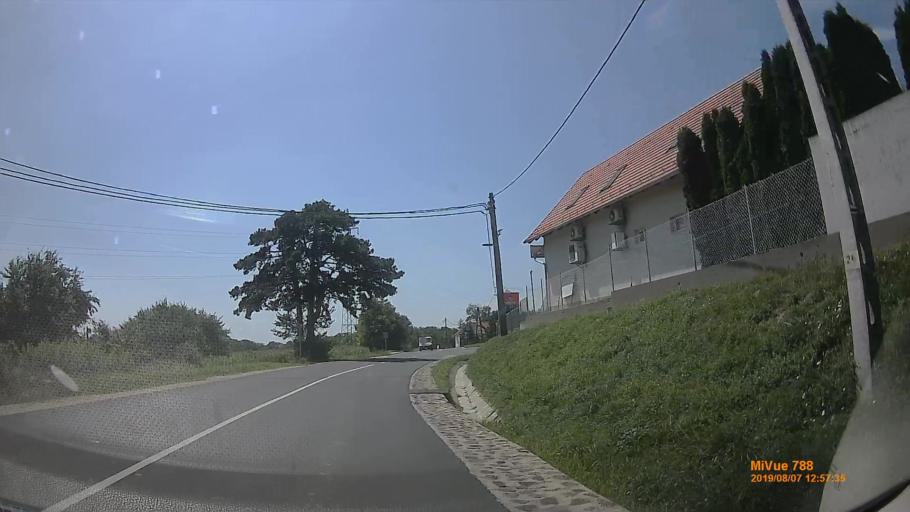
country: HU
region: Zala
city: Keszthely
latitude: 46.7873
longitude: 17.2568
